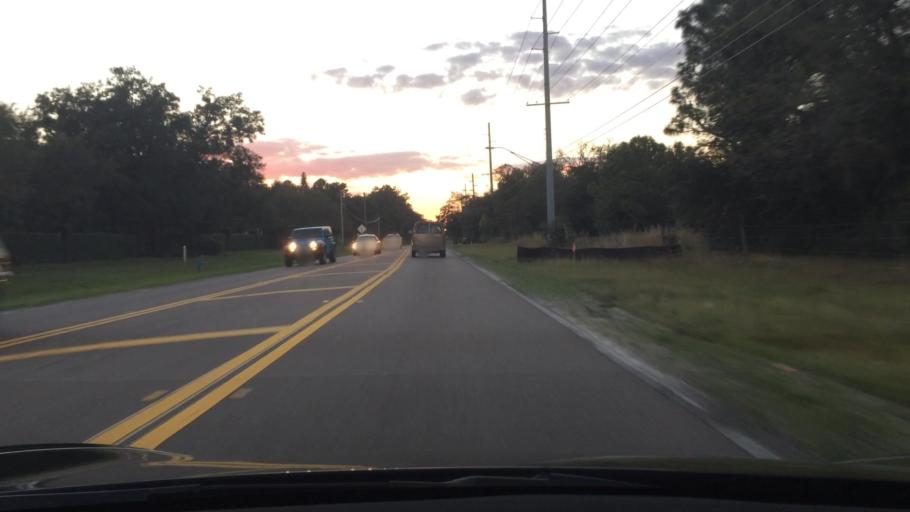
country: US
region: Florida
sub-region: Hillsborough County
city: Greater Northdale
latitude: 28.1289
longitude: -82.5556
